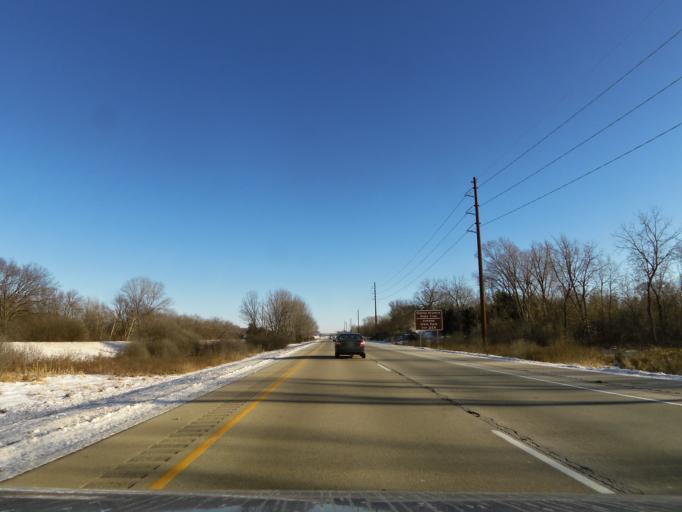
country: US
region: Wisconsin
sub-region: Jefferson County
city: Lake Mills
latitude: 43.0979
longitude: -88.9228
